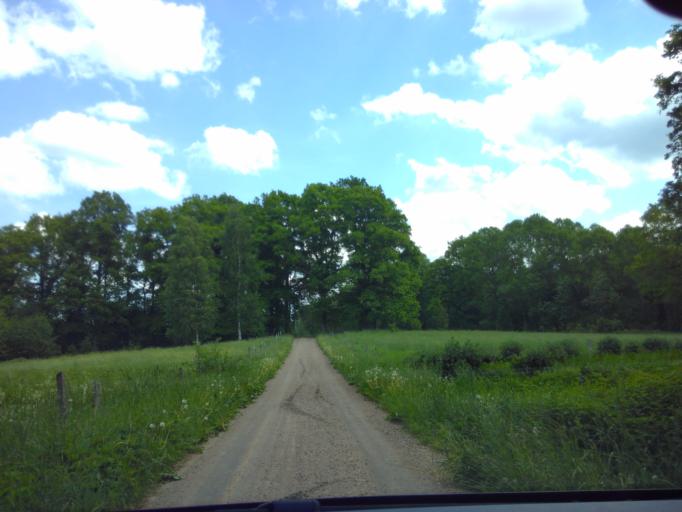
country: SE
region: Vaestra Goetaland
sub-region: Herrljunga Kommun
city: Herrljunga
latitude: 58.0734
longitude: 13.0018
